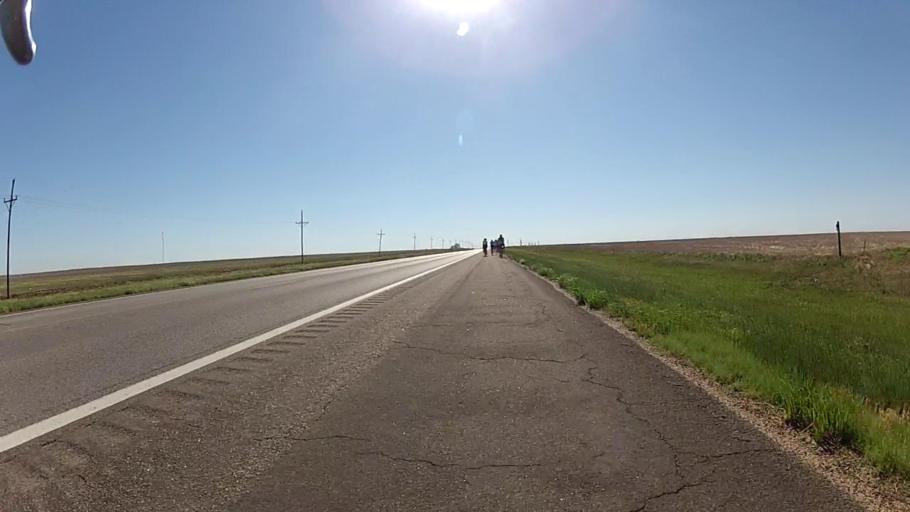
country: US
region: Kansas
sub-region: Kiowa County
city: Greensburg
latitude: 37.5863
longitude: -99.6219
